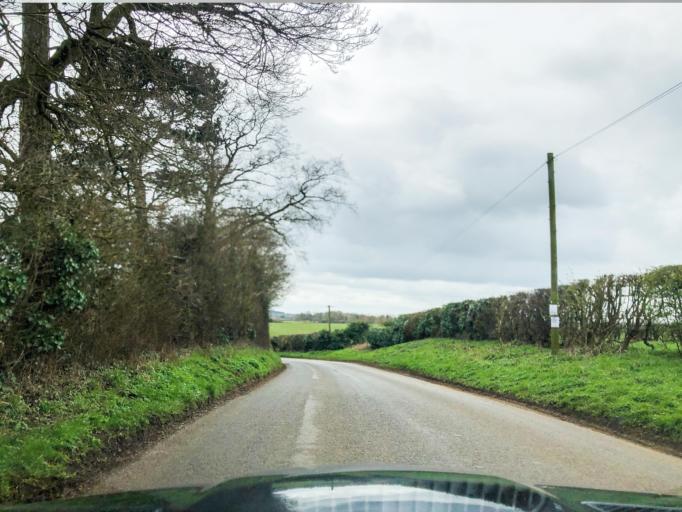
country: GB
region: England
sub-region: Oxfordshire
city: Hook Norton
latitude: 52.1030
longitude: -1.4772
